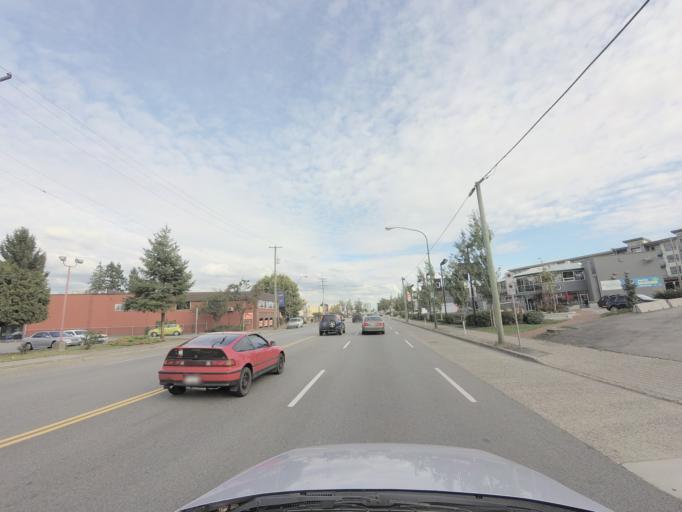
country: CA
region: British Columbia
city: Burnaby
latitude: 49.2240
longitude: -122.9860
